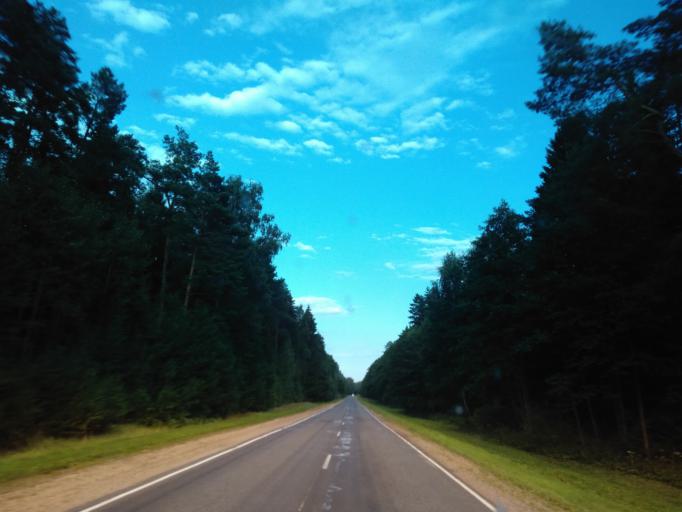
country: BY
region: Minsk
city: Uzda
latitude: 53.4243
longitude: 27.3810
